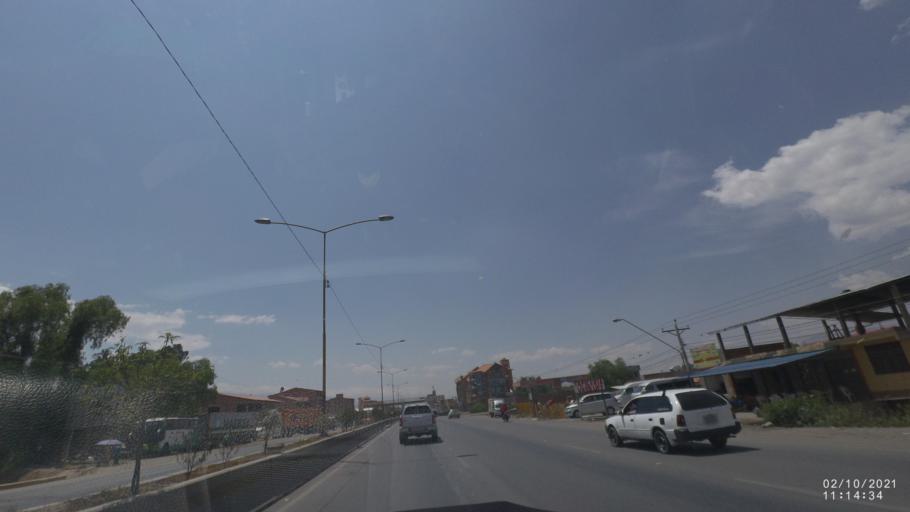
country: BO
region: Cochabamba
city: Sipe Sipe
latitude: -17.3958
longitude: -66.3110
